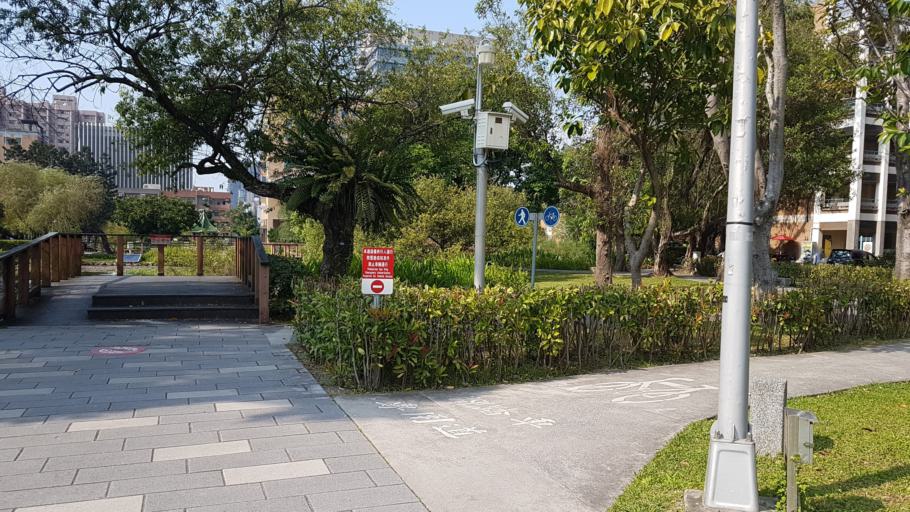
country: TW
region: Taipei
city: Taipei
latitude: 25.0192
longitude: 121.5376
